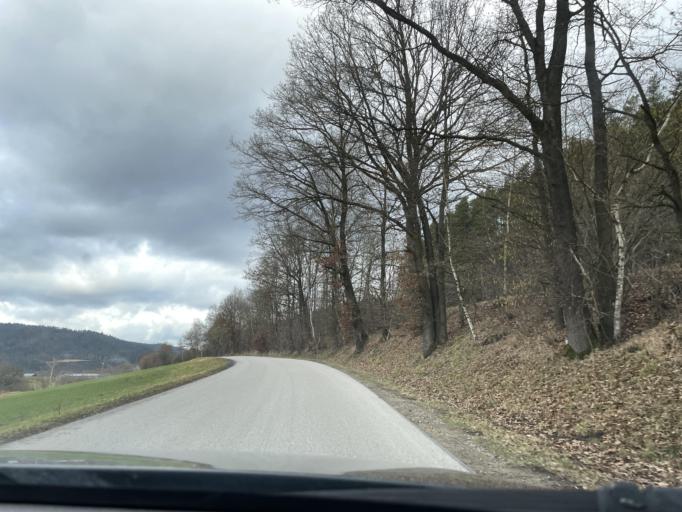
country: DE
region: Bavaria
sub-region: Upper Palatinate
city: Blaibach
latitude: 49.1514
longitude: 12.8130
